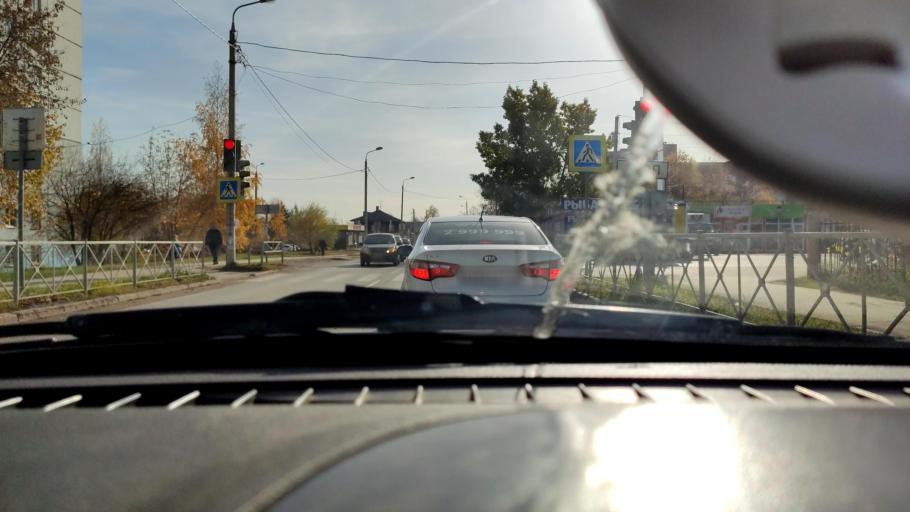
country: RU
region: Perm
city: Perm
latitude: 58.0329
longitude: 56.3251
